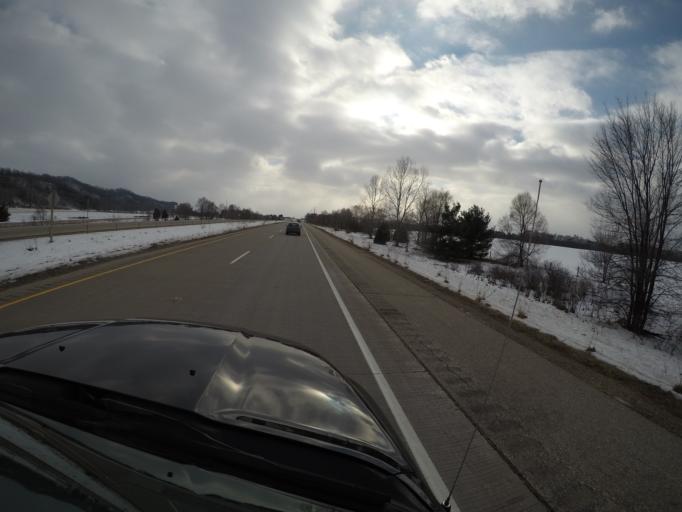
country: US
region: Wisconsin
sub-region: La Crosse County
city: Holmen
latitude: 44.0078
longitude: -91.2865
